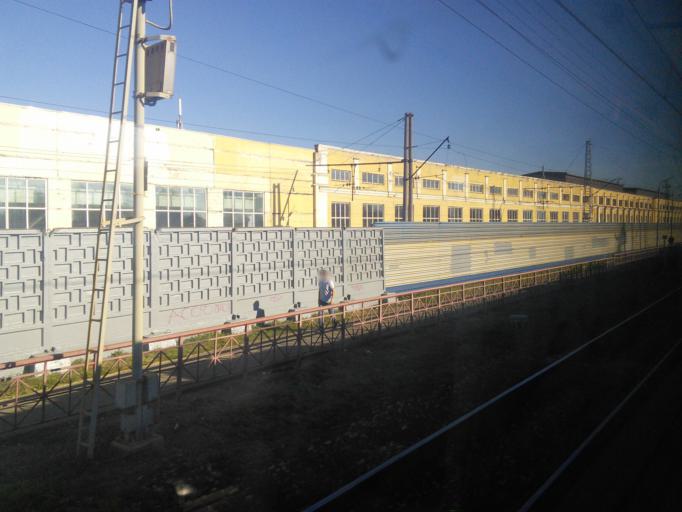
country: RU
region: Moscow
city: Mar'ino
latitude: 55.6593
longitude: 37.7138
